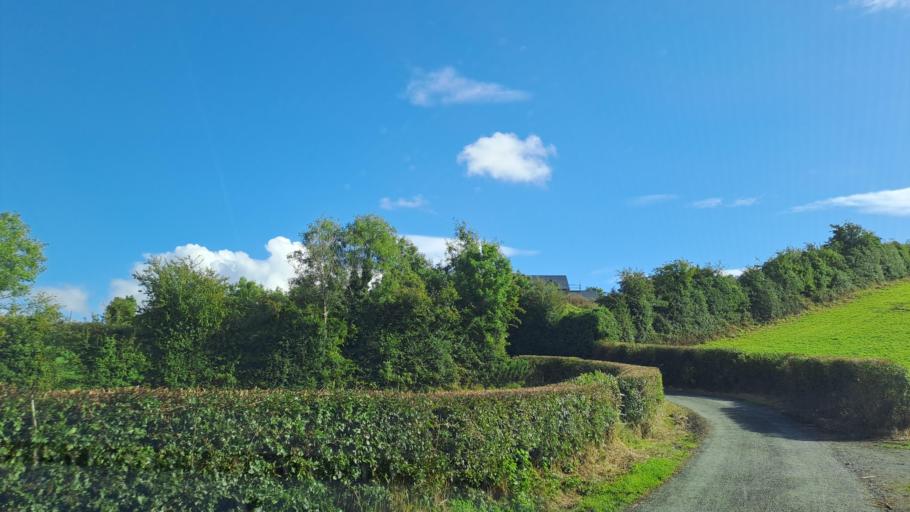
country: IE
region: Ulster
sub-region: An Cabhan
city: Kingscourt
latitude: 53.9963
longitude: -6.8731
